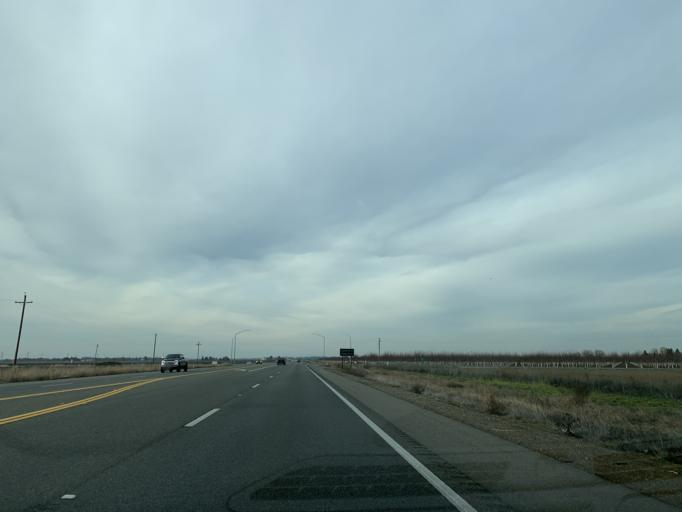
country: US
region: California
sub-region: Yuba County
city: Plumas Lake
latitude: 38.8649
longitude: -121.5535
